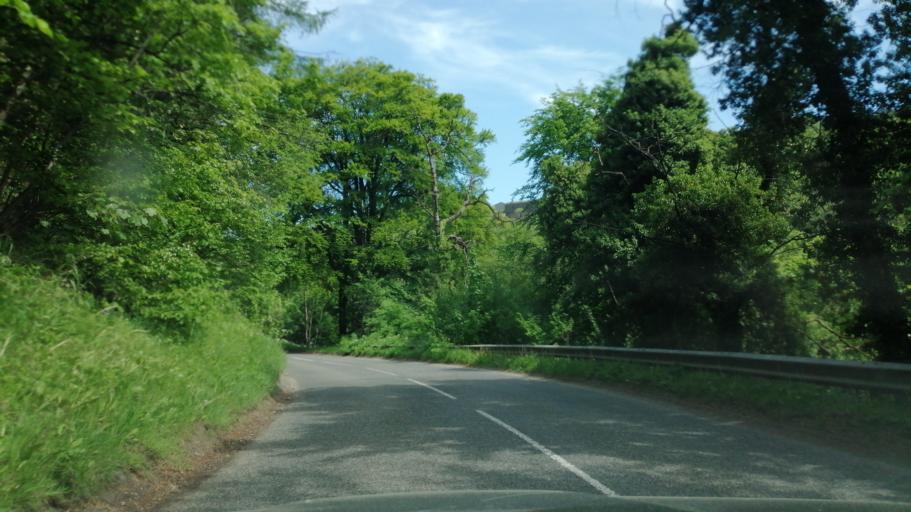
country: GB
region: Scotland
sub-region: Moray
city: Dufftown
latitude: 57.4508
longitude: -3.1212
